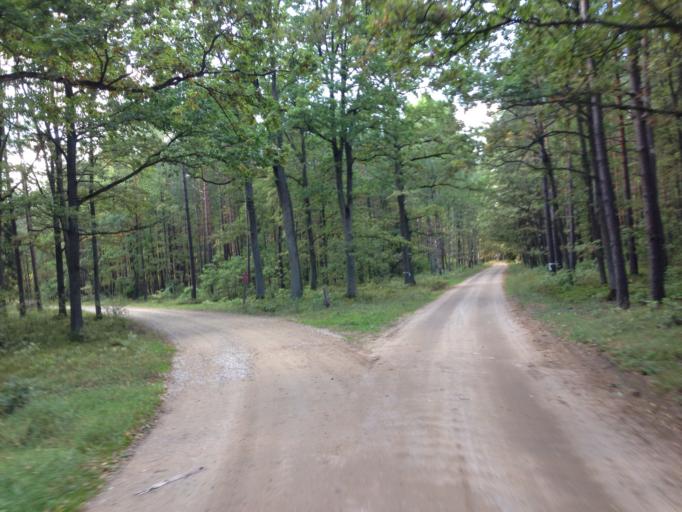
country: PL
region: Kujawsko-Pomorskie
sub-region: Powiat brodnicki
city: Gorzno
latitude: 53.1833
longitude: 19.7428
